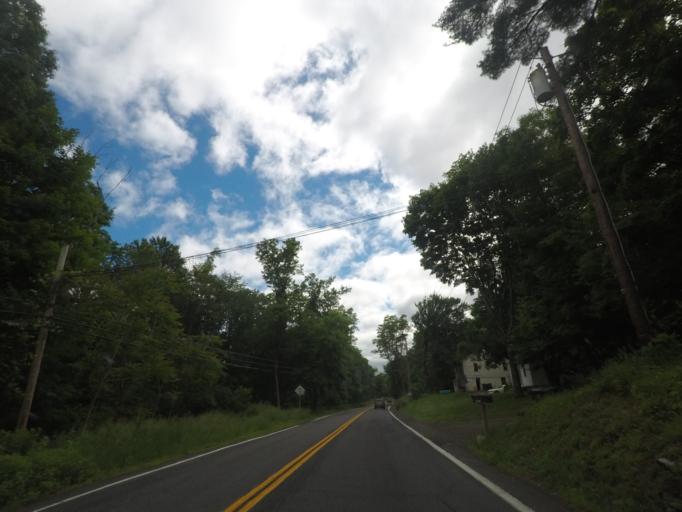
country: US
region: New York
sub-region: Columbia County
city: Philmont
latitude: 42.2489
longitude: -73.6738
